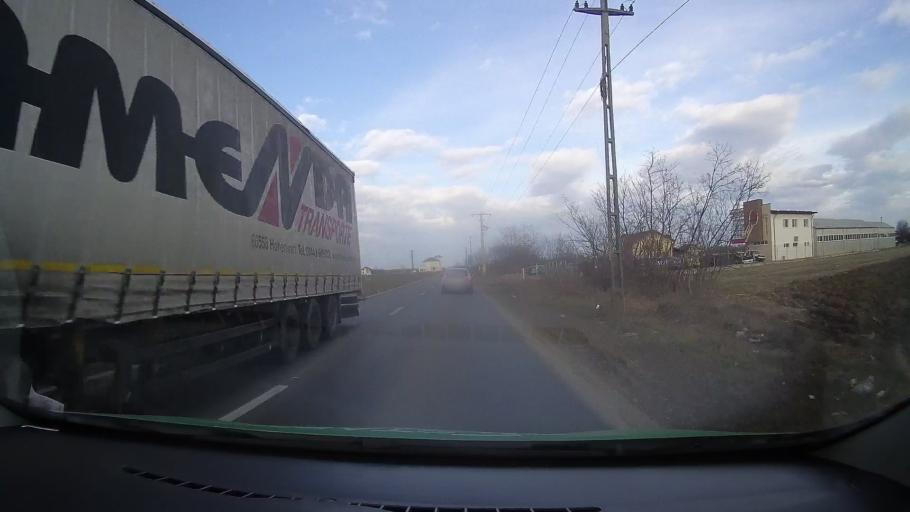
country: RO
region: Dambovita
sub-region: Comuna Ulmi
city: Ulmi
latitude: 44.8965
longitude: 25.5130
